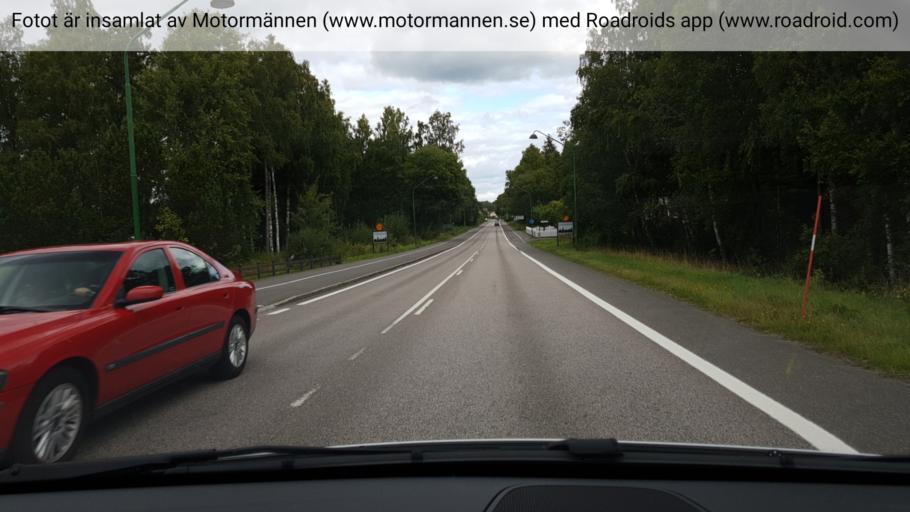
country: SE
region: Vaestra Goetaland
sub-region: Tidaholms Kommun
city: Tidaholm
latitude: 58.1674
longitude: 13.9432
